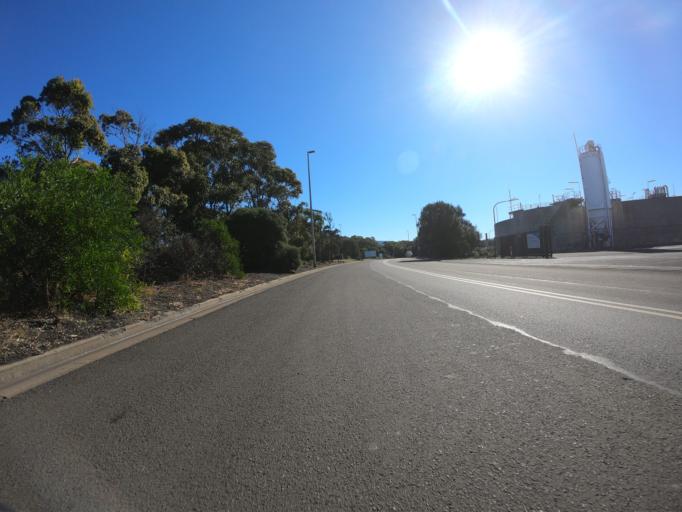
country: AU
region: New South Wales
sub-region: Wollongong
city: Coniston
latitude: -34.4439
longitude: 150.8970
